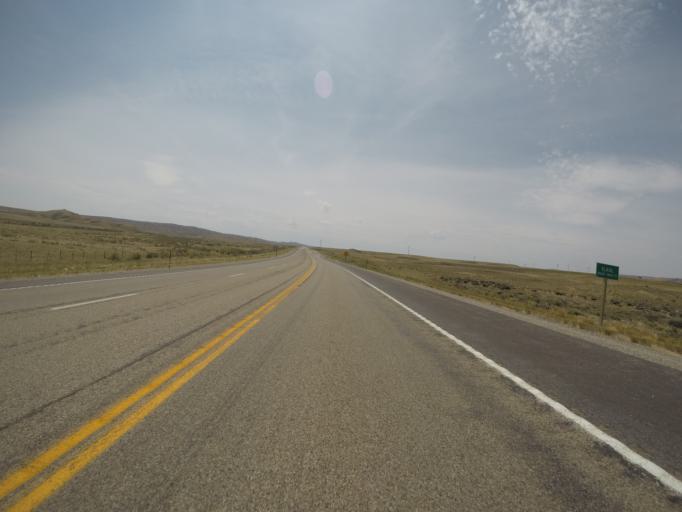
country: US
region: Wyoming
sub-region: Lincoln County
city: Kemmerer
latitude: 41.7515
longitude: -110.5654
